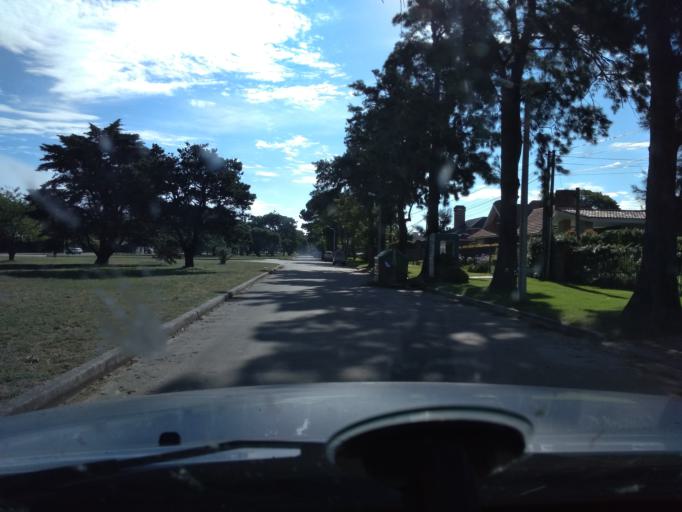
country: UY
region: Canelones
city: Paso de Carrasco
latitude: -34.8877
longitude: -56.0673
